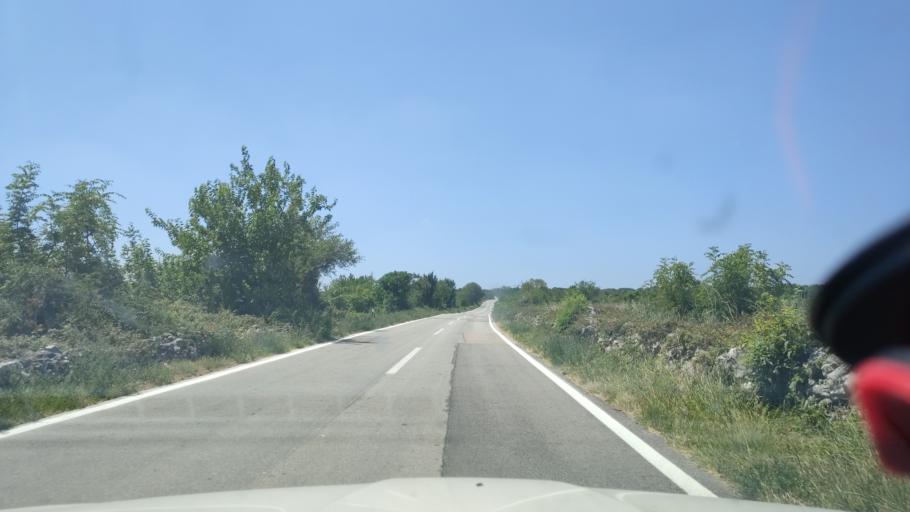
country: HR
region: Sibensko-Kniniska
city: Kistanje
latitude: 44.0116
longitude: 16.0078
